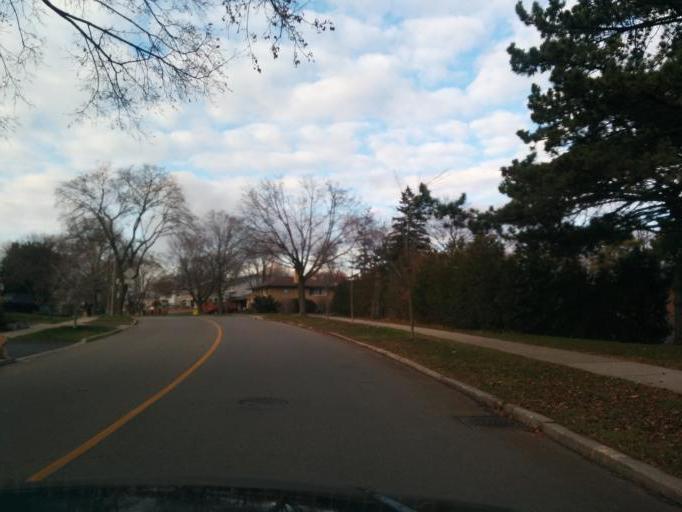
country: CA
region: Ontario
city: Etobicoke
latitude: 43.6826
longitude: -79.5459
